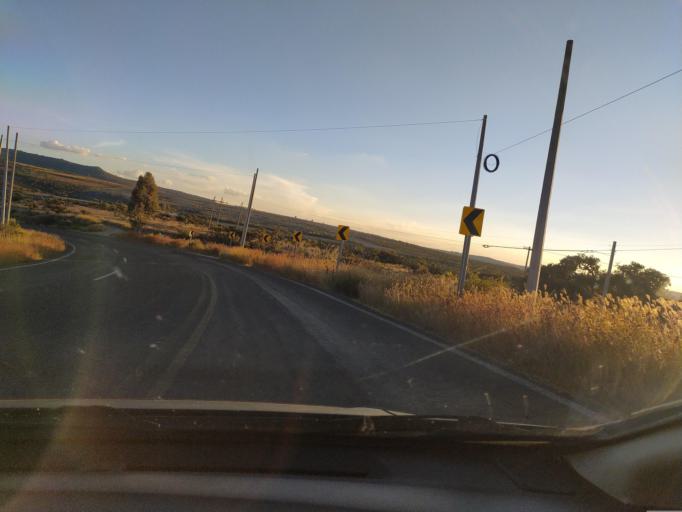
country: MX
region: Jalisco
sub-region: San Julian
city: Colonia Veintitres de Mayo
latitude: 21.0082
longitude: -102.2730
